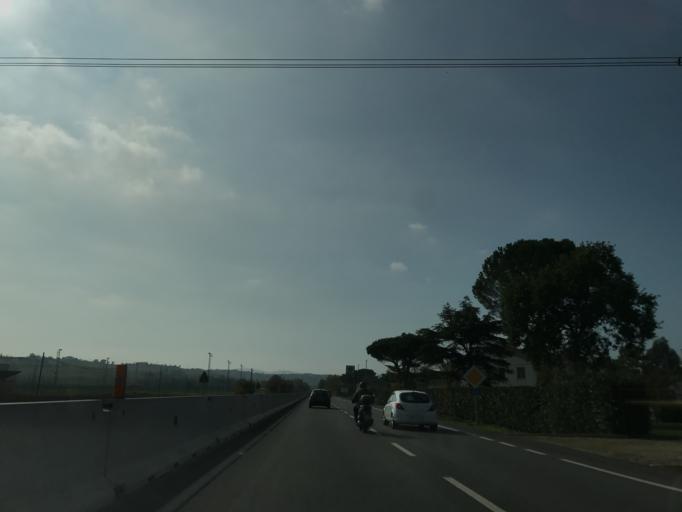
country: IT
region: Emilia-Romagna
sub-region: Provincia di Rimini
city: Cerasolo
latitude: 44.0120
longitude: 12.5462
